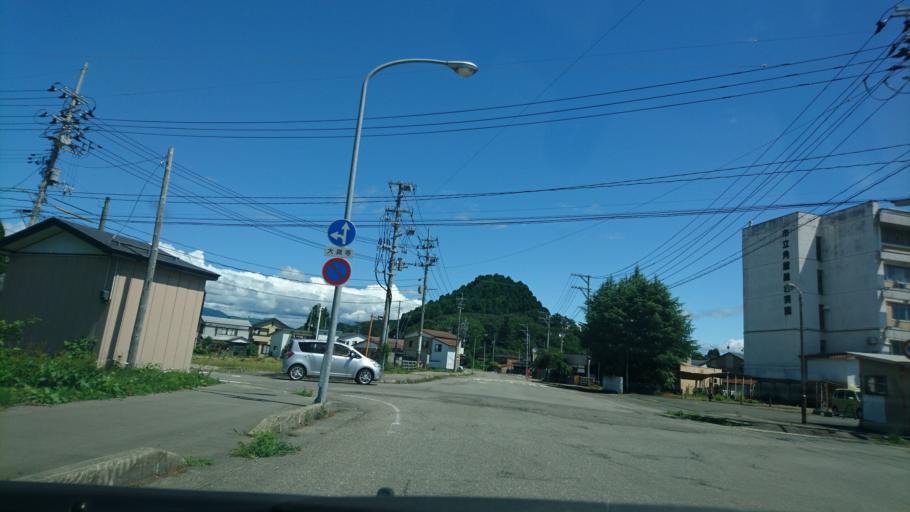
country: JP
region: Akita
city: Kakunodatemachi
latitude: 39.5854
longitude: 140.5653
